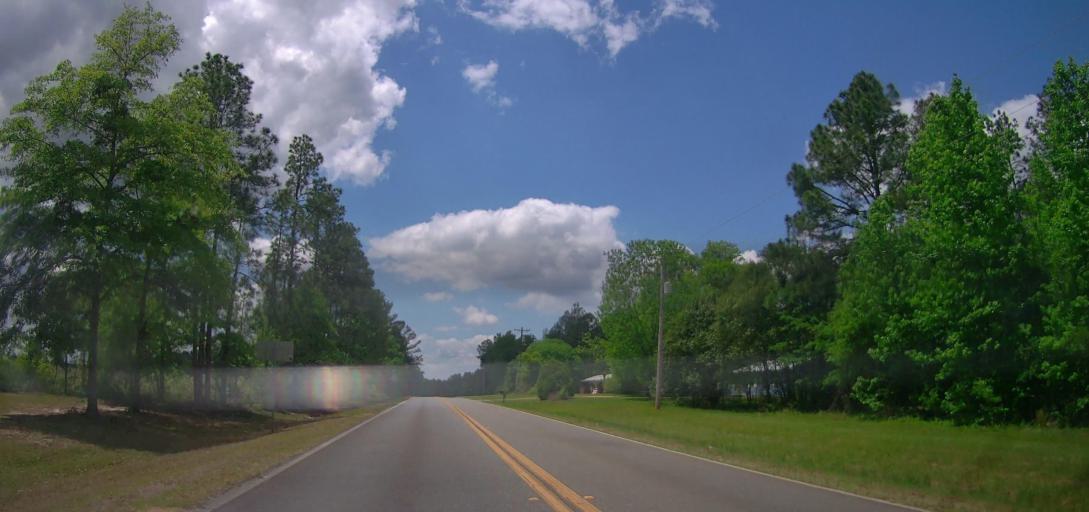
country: US
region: Georgia
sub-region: Laurens County
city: East Dublin
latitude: 32.5254
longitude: -82.7472
